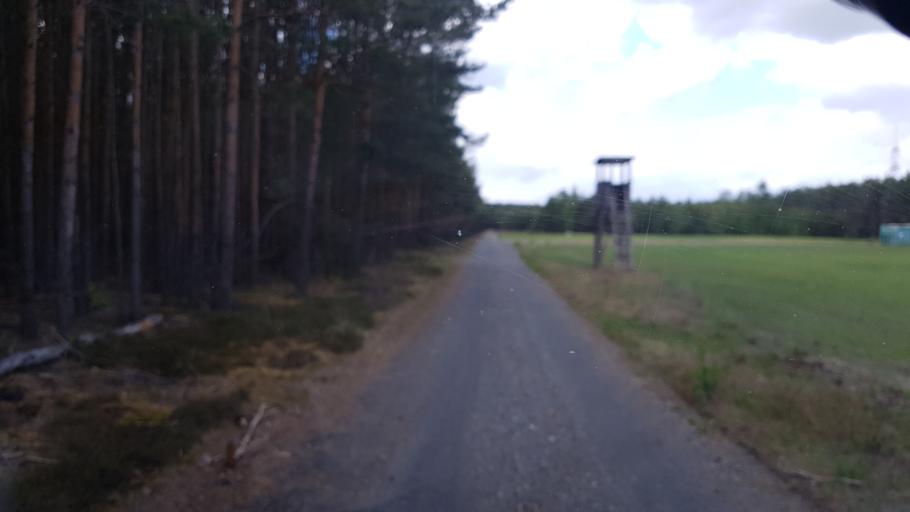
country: DE
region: Brandenburg
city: Altdobern
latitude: 51.6335
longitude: 13.9838
